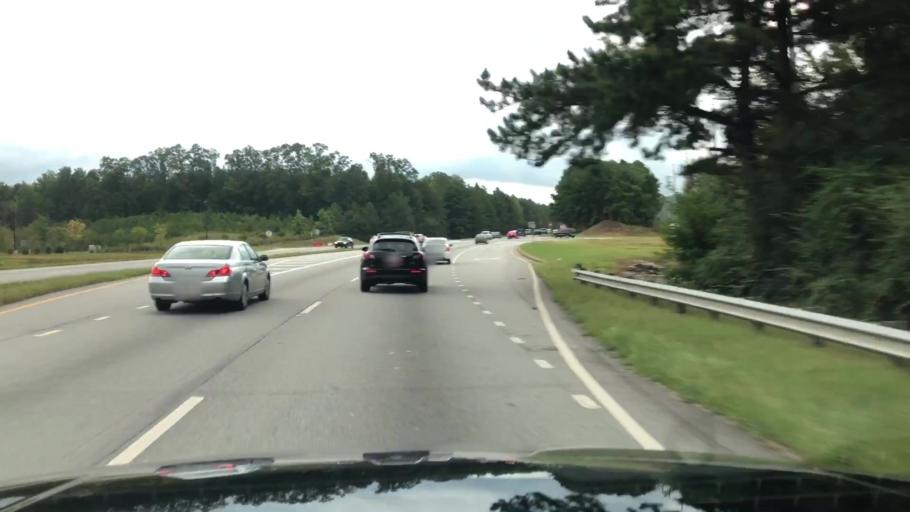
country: US
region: Georgia
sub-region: Cobb County
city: Mableton
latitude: 33.7441
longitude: -84.5892
